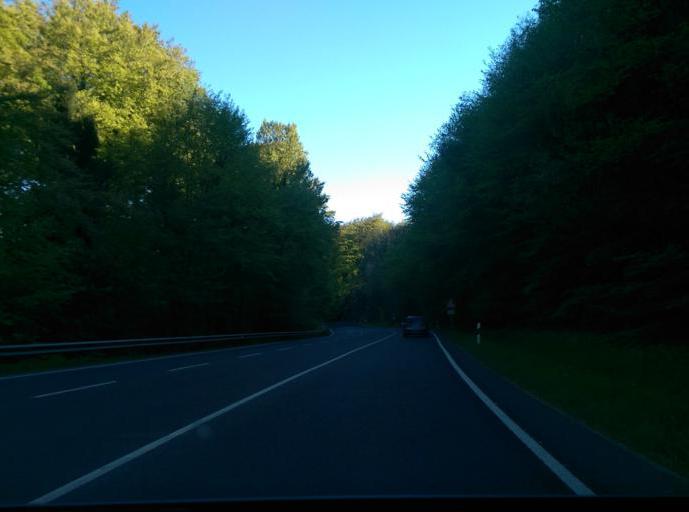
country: LU
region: Luxembourg
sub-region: Canton de Luxembourg
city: Niederanven
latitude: 49.6441
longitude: 6.2337
